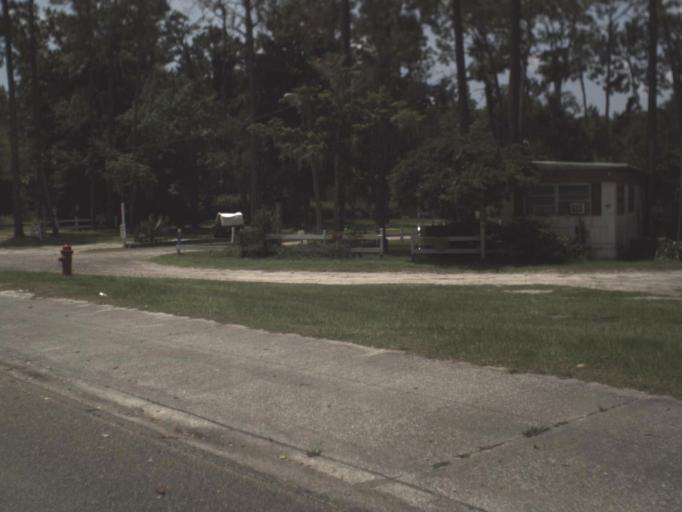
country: US
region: Florida
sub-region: Taylor County
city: Perry
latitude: 30.0847
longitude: -83.5694
